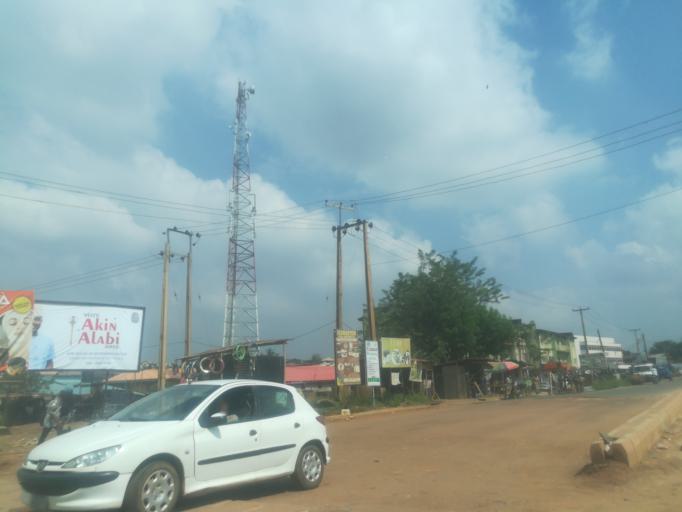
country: NG
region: Oyo
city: Ibadan
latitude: 7.3912
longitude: 3.9467
